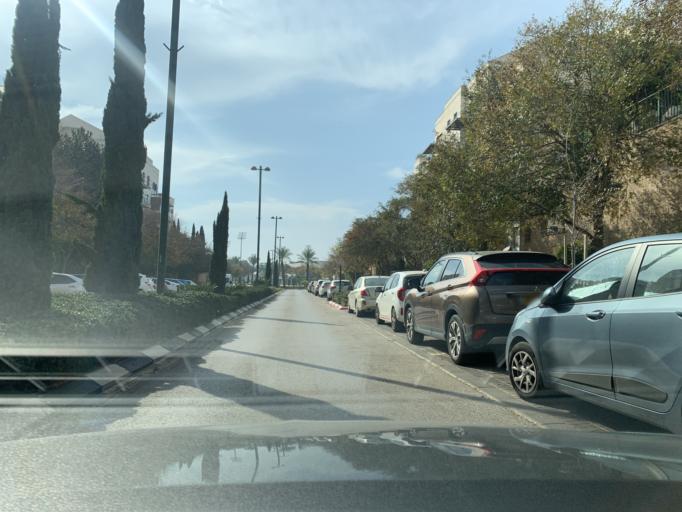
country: IL
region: Central District
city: Kfar Saba
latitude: 32.1861
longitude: 34.9283
